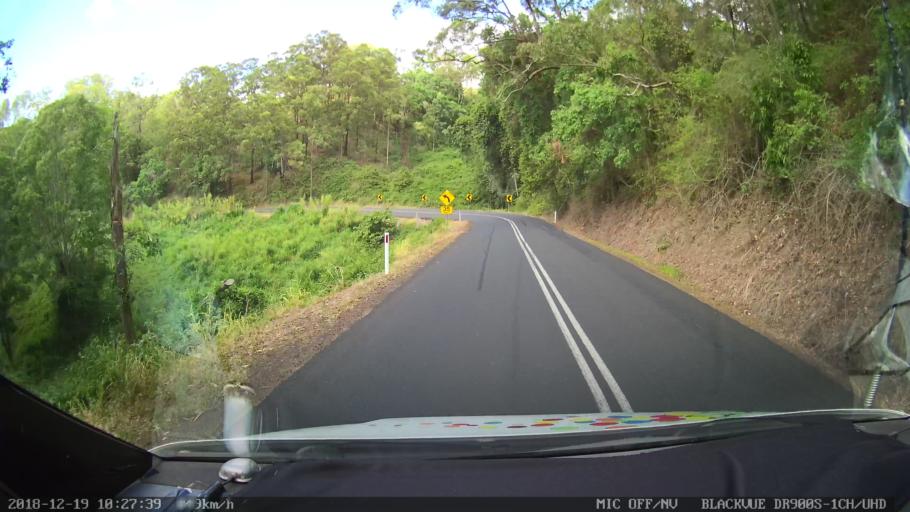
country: AU
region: New South Wales
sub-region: Lismore Municipality
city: Larnook
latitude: -28.5994
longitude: 153.0927
